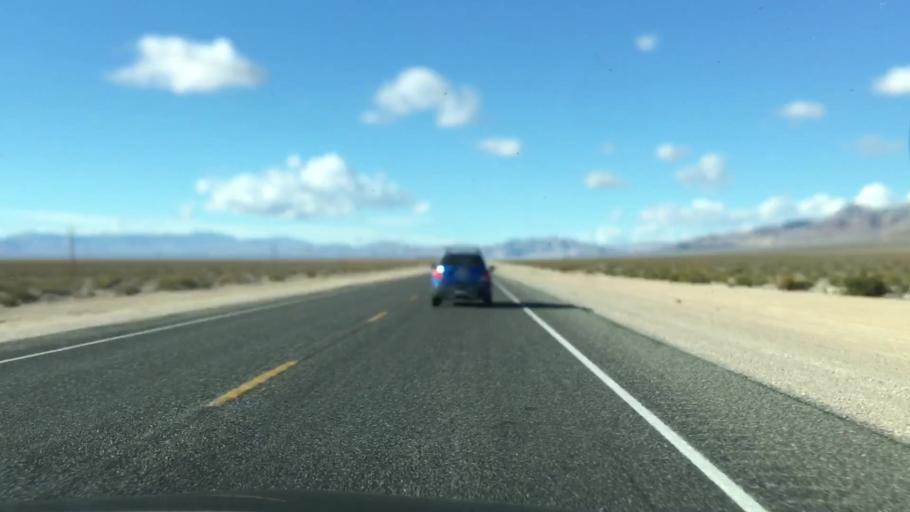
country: US
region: Nevada
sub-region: Nye County
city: Beatty
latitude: 36.7343
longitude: -116.6366
